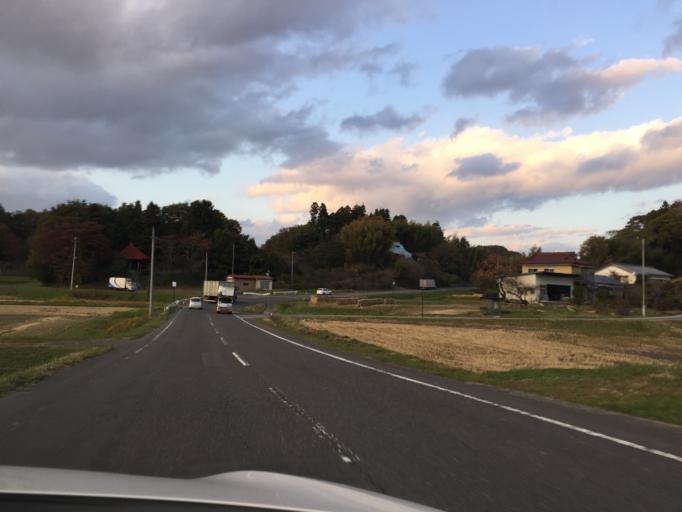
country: JP
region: Fukushima
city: Miharu
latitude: 37.4697
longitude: 140.4408
